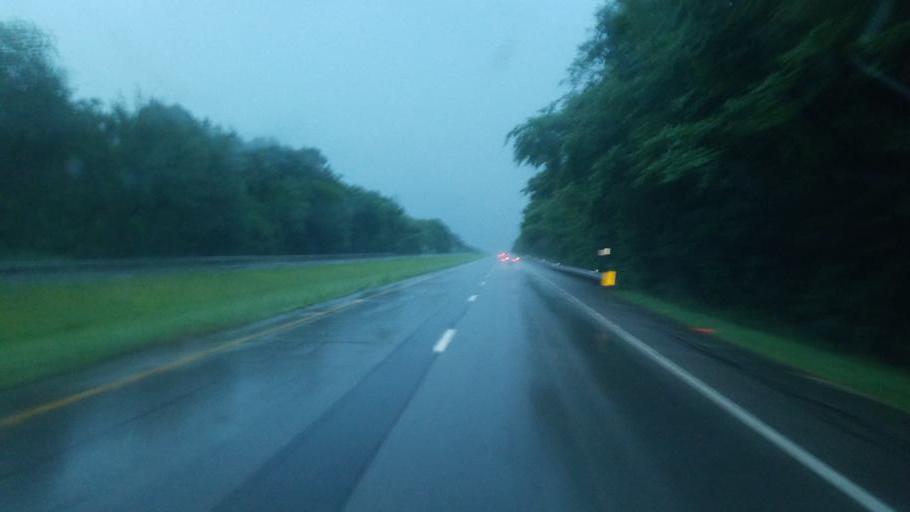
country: US
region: Ohio
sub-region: Summit County
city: Clinton
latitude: 40.9005
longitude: -81.6425
